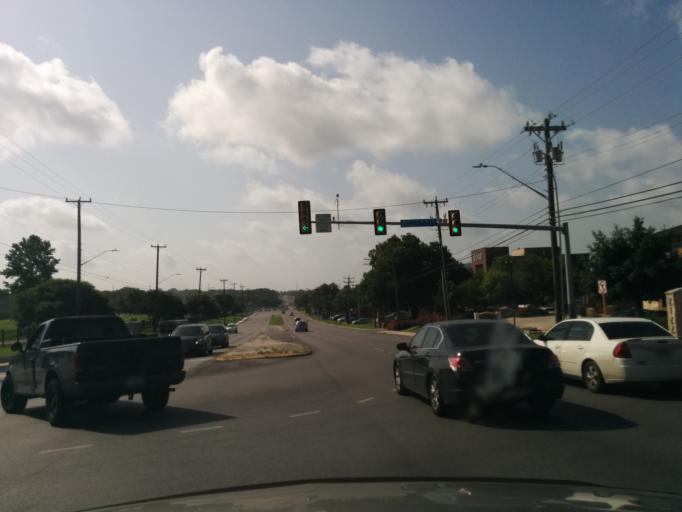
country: US
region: Texas
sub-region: Bexar County
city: Balcones Heights
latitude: 29.5026
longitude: -98.5816
